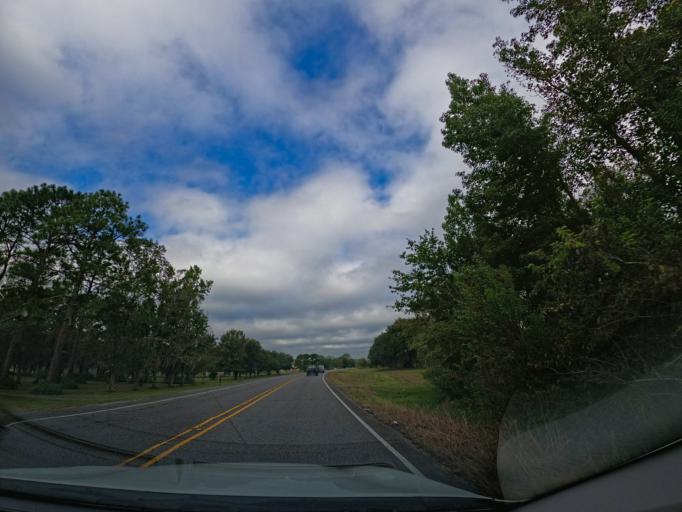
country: US
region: Louisiana
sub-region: Terrebonne Parish
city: Gray
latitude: 29.6086
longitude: -90.8900
